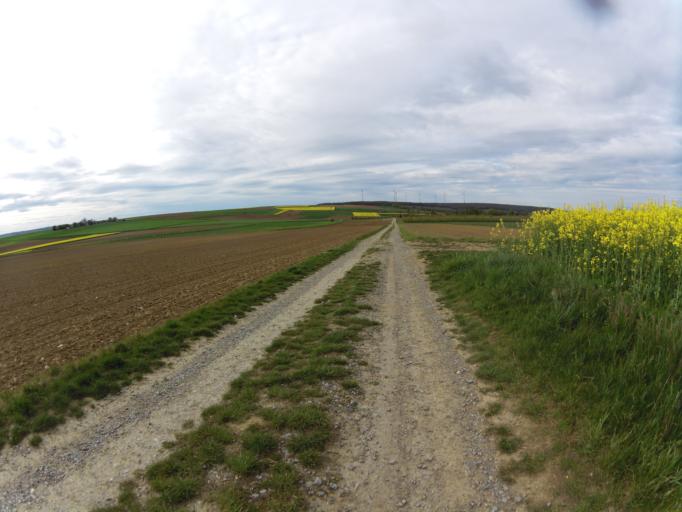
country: DE
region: Bavaria
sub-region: Regierungsbezirk Unterfranken
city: Prosselsheim
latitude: 49.8631
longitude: 10.1516
